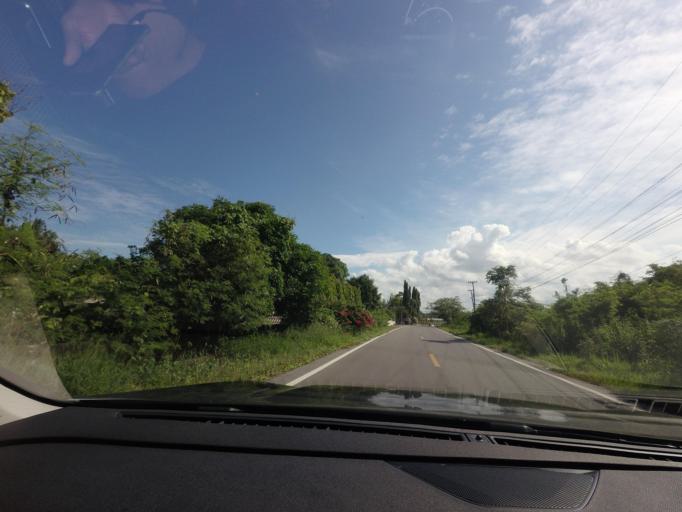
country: TH
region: Prachuap Khiri Khan
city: Pran Buri
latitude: 12.4607
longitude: 99.9455
